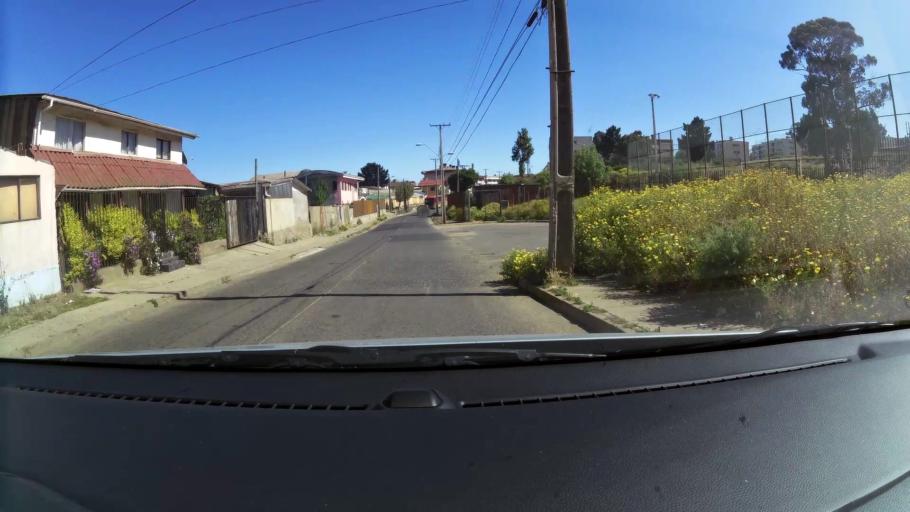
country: CL
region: Valparaiso
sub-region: Provincia de Valparaiso
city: Valparaiso
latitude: -33.0523
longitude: -71.6516
